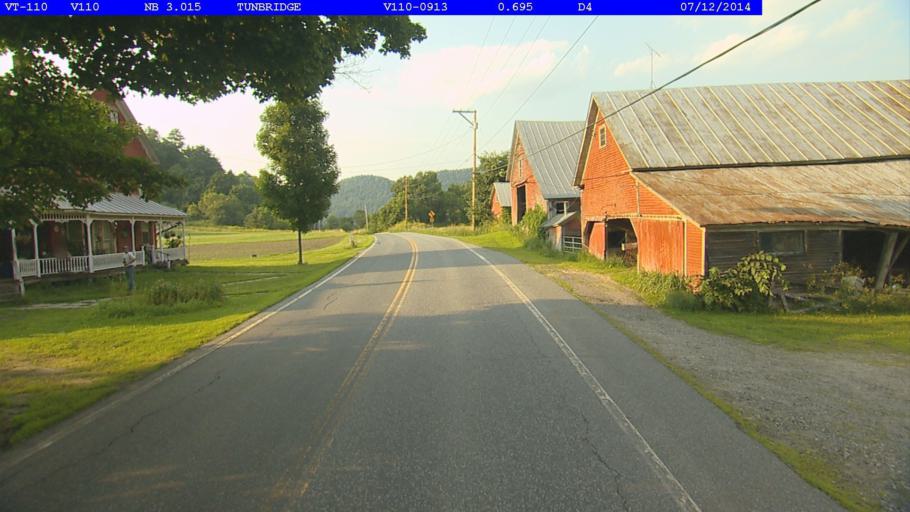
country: US
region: Vermont
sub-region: Orange County
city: Chelsea
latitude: 43.8609
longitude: -72.4999
